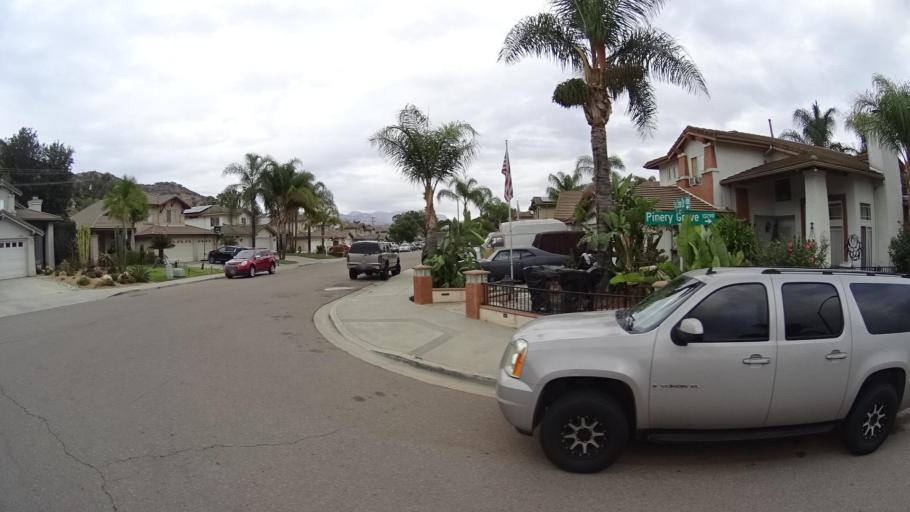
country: US
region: California
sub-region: San Diego County
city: Eucalyptus Hills
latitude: 32.8608
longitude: -116.9521
